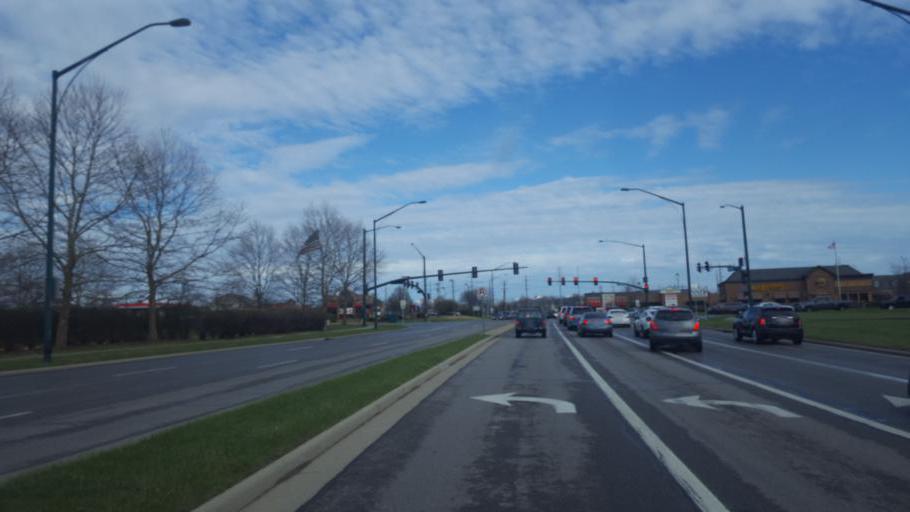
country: US
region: Ohio
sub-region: Franklin County
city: Westerville
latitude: 40.1472
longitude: -82.9250
